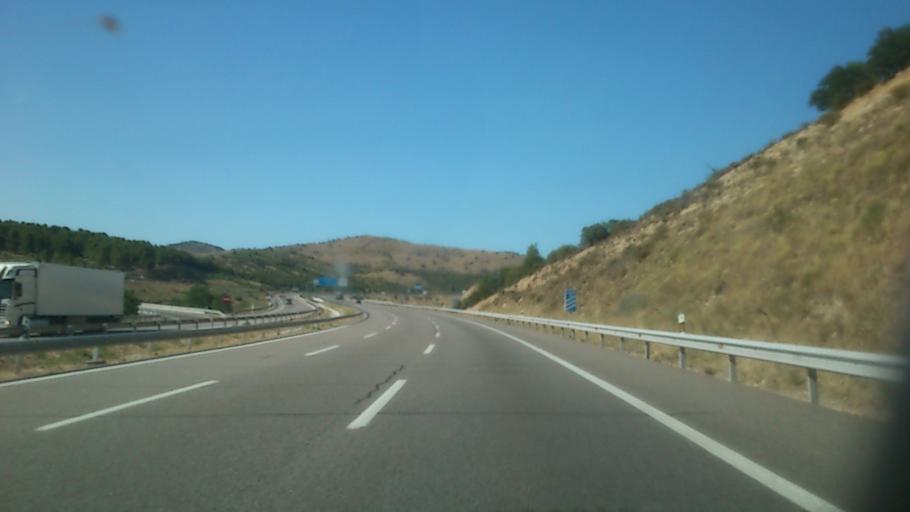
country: ES
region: Aragon
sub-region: Provincia de Zaragoza
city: Paracuellos de la Ribera
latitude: 41.3757
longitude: -1.5722
